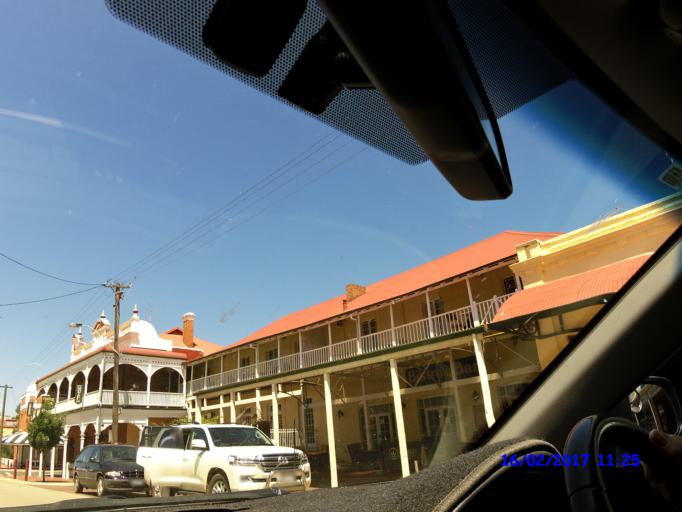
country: AU
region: Western Australia
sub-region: York
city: York
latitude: -31.8893
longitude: 116.7687
